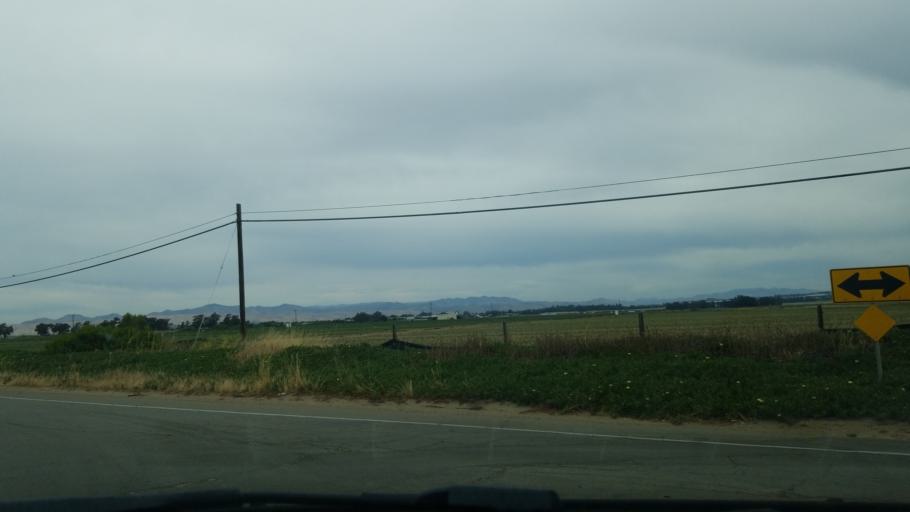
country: US
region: California
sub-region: Santa Barbara County
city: Orcutt
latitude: 34.9092
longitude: -120.4896
